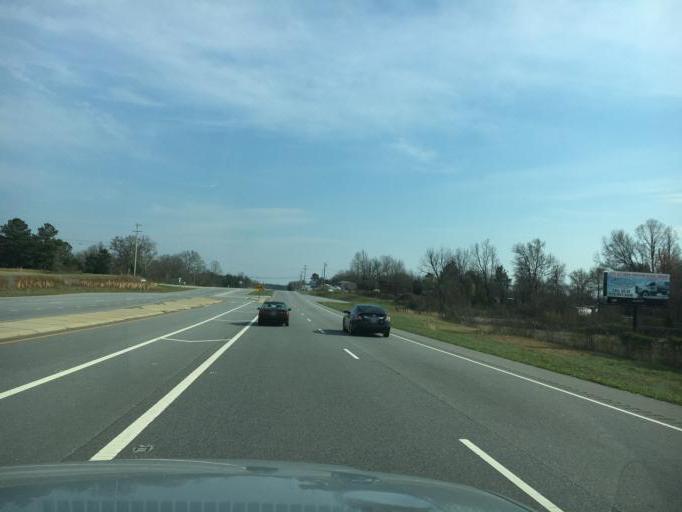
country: US
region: North Carolina
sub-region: Rutherford County
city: Forest City
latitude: 35.2955
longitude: -81.9117
